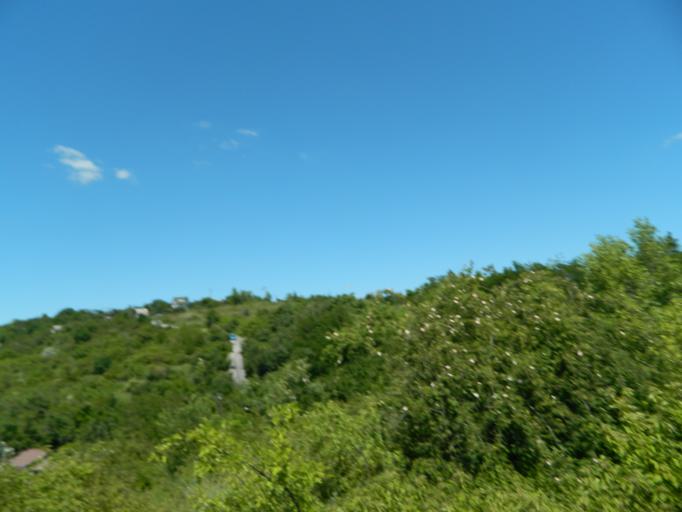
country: HU
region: Pest
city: Budakalasz
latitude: 47.6055
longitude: 19.0534
